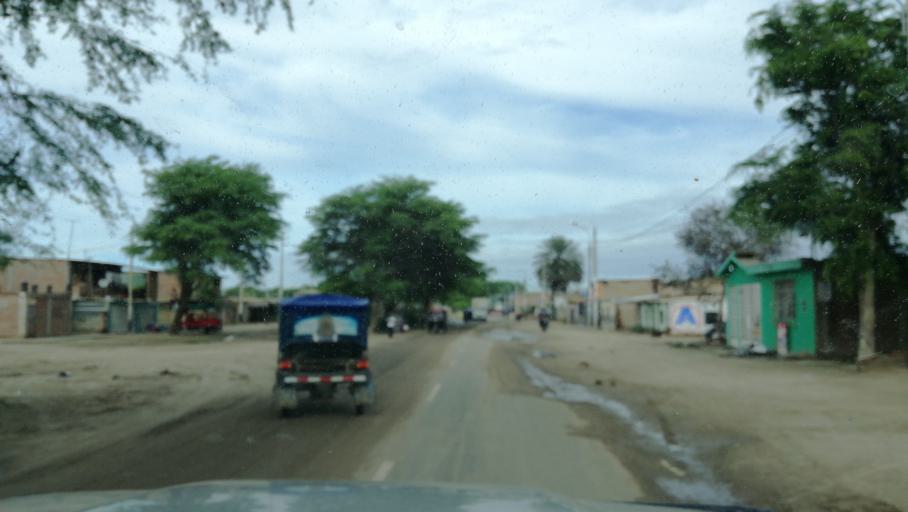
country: PE
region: Piura
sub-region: Provincia de Piura
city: Piura
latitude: -5.1863
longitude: -80.6741
